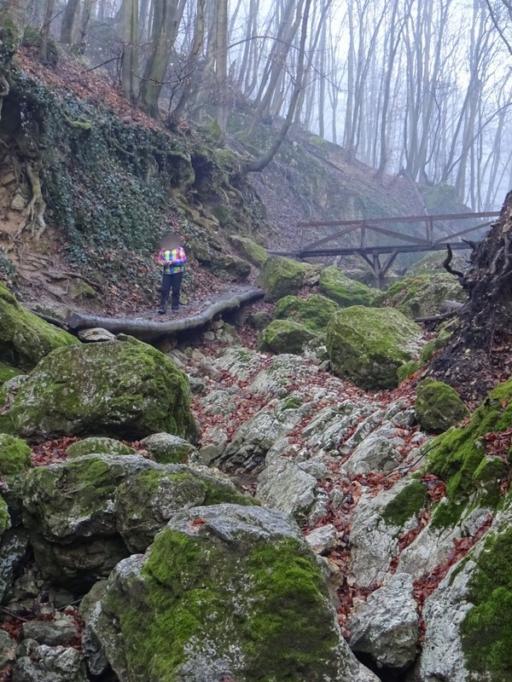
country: HU
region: Pest
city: Pilisszentkereszt
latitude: 47.6846
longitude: 18.9163
